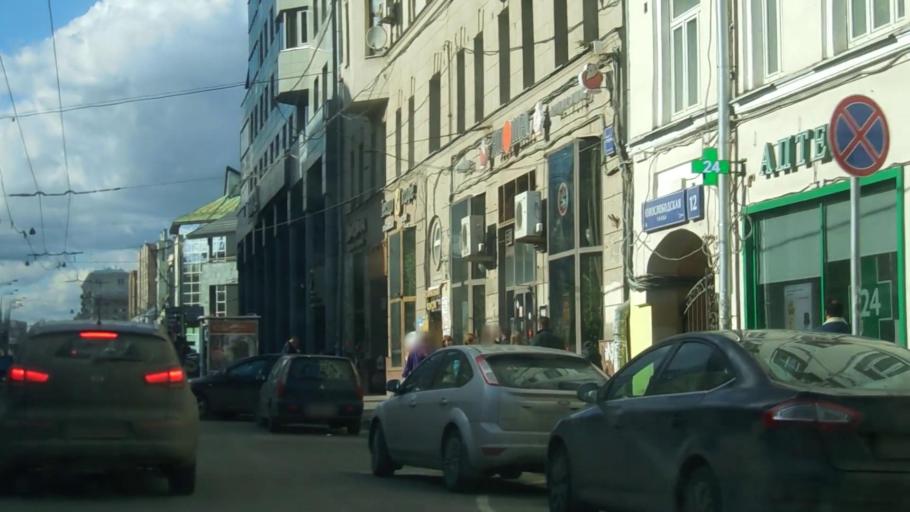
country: RU
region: Moscow
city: Mar'ina Roshcha
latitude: 55.7805
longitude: 37.6000
